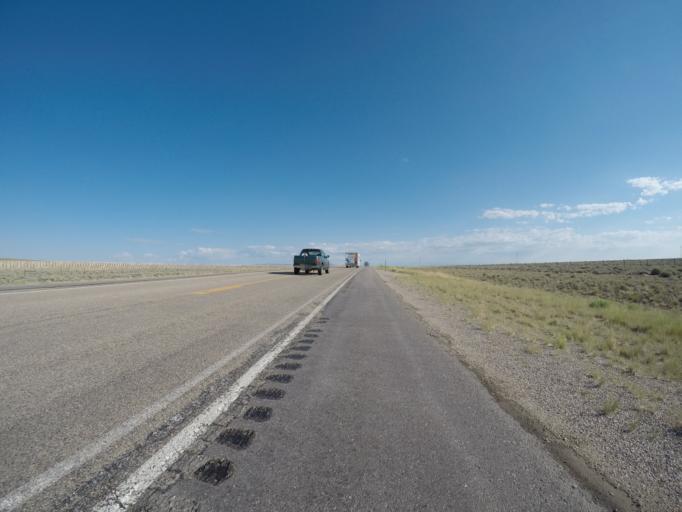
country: US
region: Wyoming
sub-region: Lincoln County
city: Kemmerer
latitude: 42.0504
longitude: -110.1624
